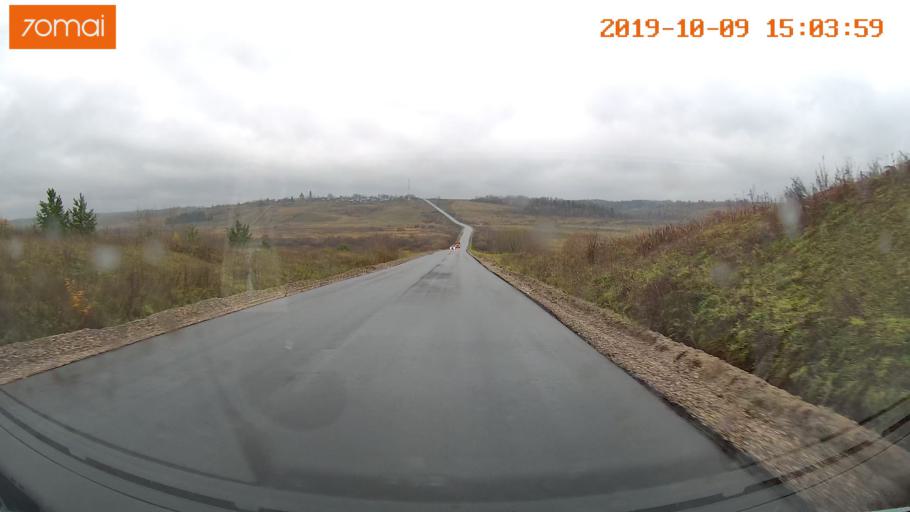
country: RU
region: Kostroma
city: Chistyye Bory
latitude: 58.2642
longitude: 41.6713
